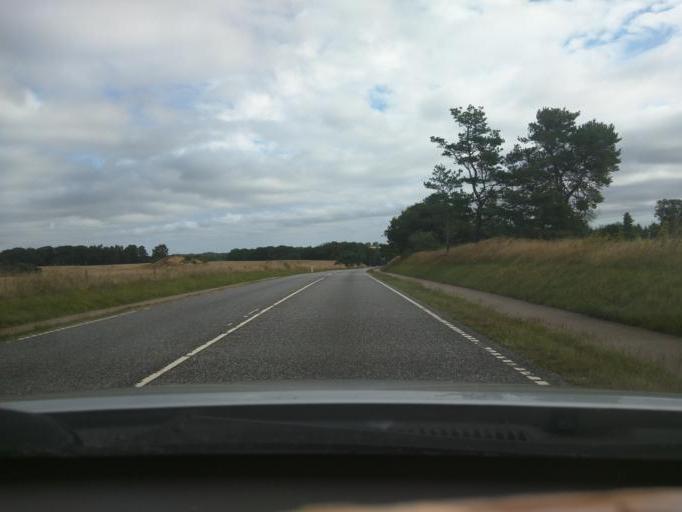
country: DK
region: Central Jutland
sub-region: Silkeborg Kommune
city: Kjellerup
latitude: 56.3526
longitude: 9.3590
